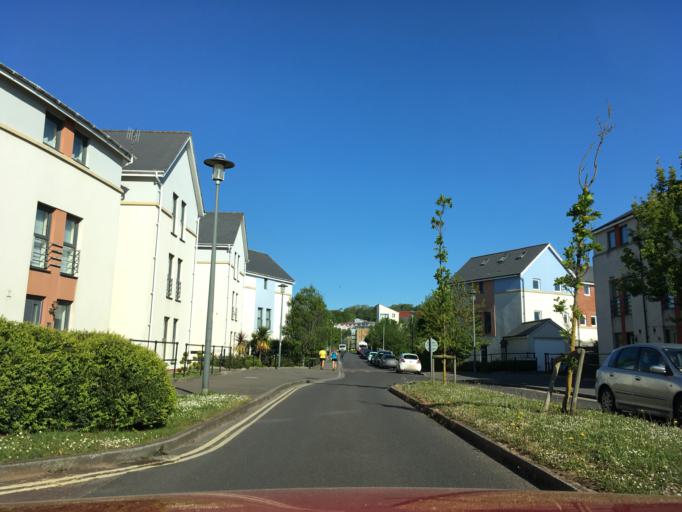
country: GB
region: England
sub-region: North Somerset
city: Portishead
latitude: 51.4886
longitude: -2.7549
